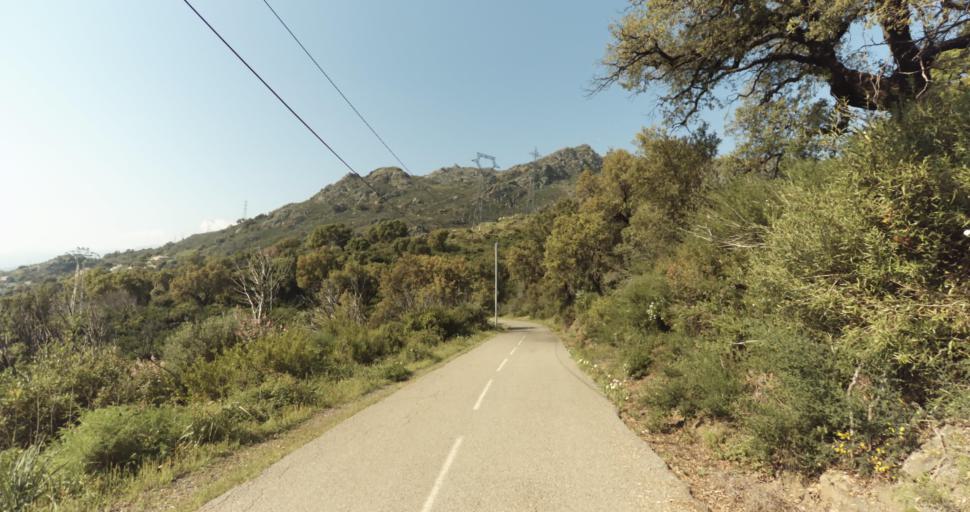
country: FR
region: Corsica
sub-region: Departement de la Haute-Corse
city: Biguglia
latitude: 42.6369
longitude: 9.4168
